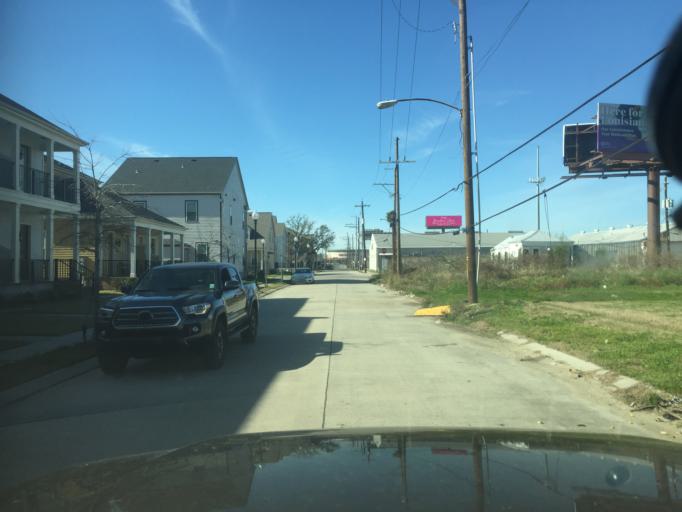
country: US
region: Louisiana
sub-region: Orleans Parish
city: New Orleans
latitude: 29.9455
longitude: -90.0813
